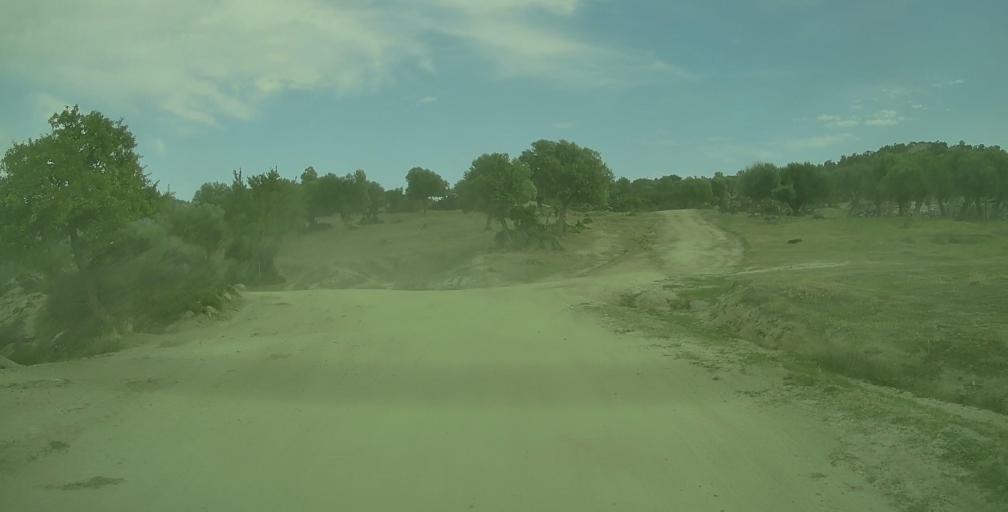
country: GR
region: Central Macedonia
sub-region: Nomos Chalkidikis
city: Sykia
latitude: 40.0138
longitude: 23.9346
